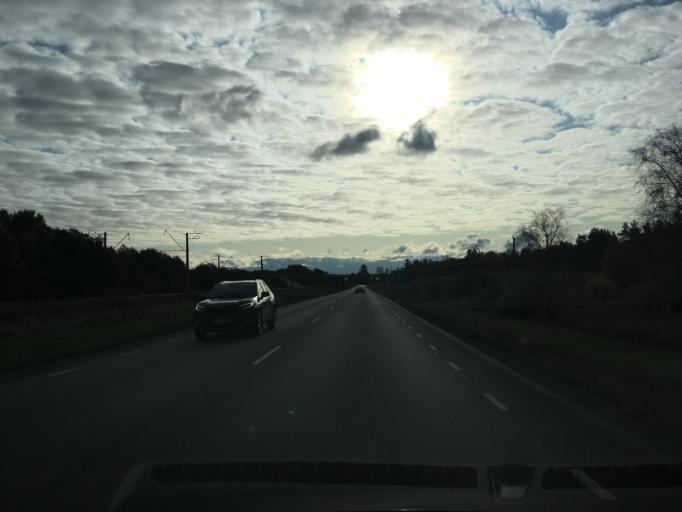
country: EE
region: Harju
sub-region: Joelaehtme vald
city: Loo
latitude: 59.4105
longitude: 24.9099
